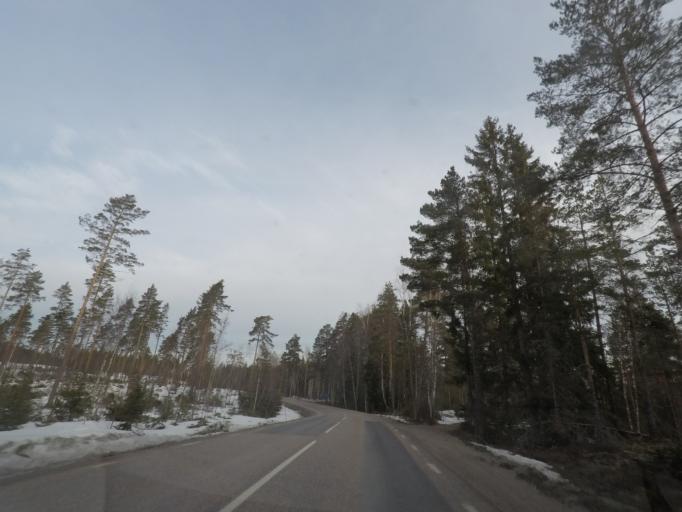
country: SE
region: Vaestmanland
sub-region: Surahammars Kommun
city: Surahammar
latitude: 59.7631
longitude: 16.2929
